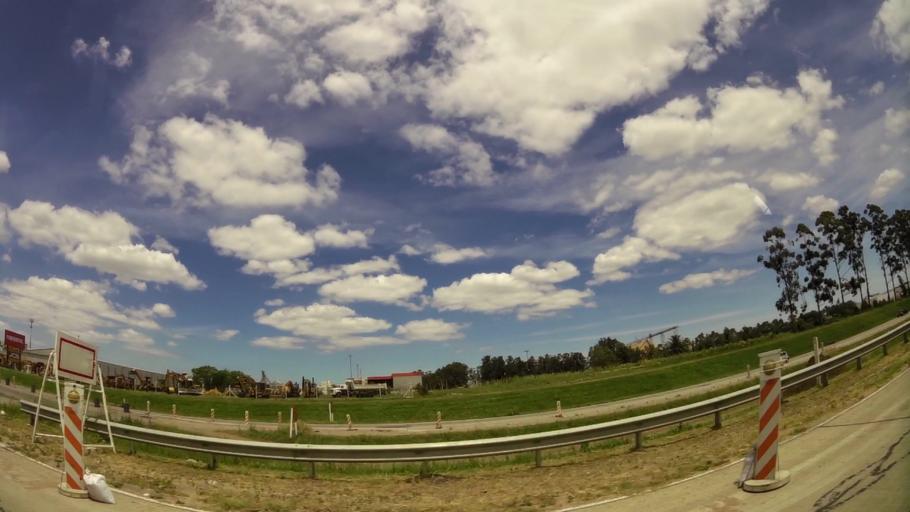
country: UY
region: Montevideo
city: Pajas Blancas
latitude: -34.8534
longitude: -56.2789
